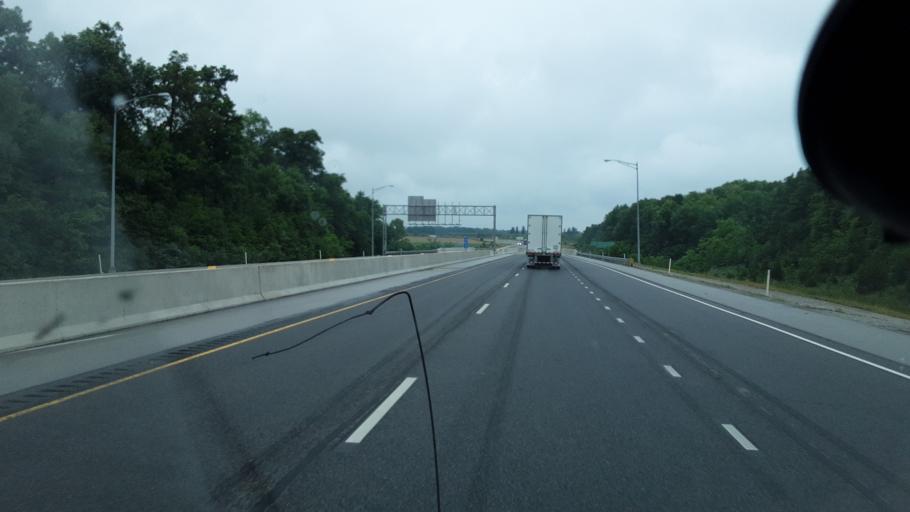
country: US
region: Indiana
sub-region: Allen County
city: New Haven
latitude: 40.9824
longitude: -85.0921
